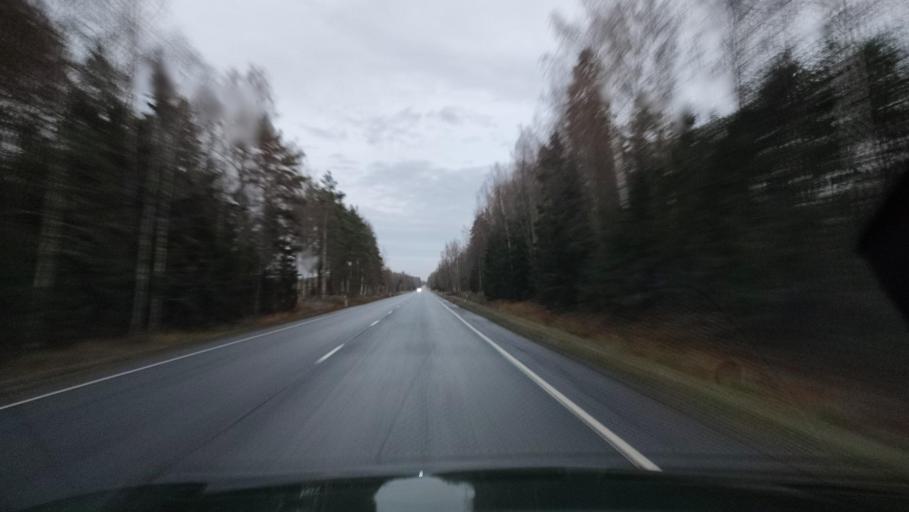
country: FI
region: Ostrobothnia
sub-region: Vaasa
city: Ristinummi
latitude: 62.9976
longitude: 21.7650
